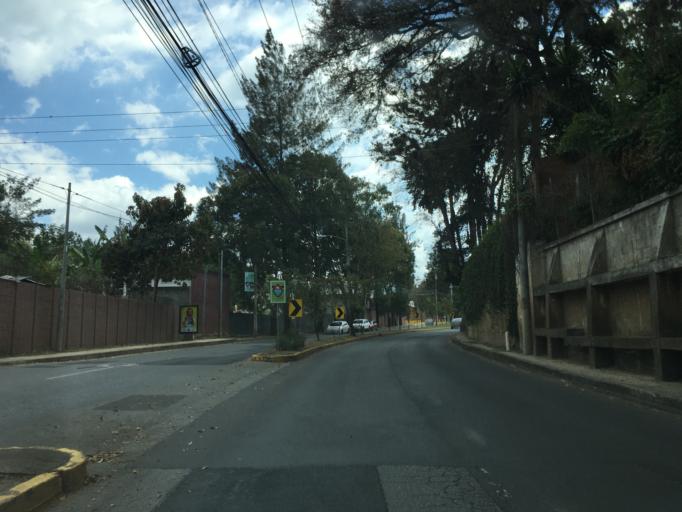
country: GT
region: Guatemala
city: Guatemala City
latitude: 14.6131
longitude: -90.4717
